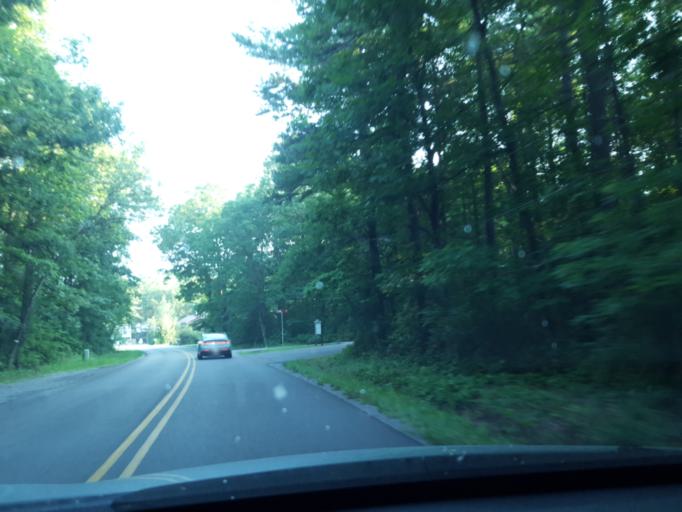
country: US
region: Virginia
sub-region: Augusta County
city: Lyndhurst
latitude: 37.9627
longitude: -78.9616
